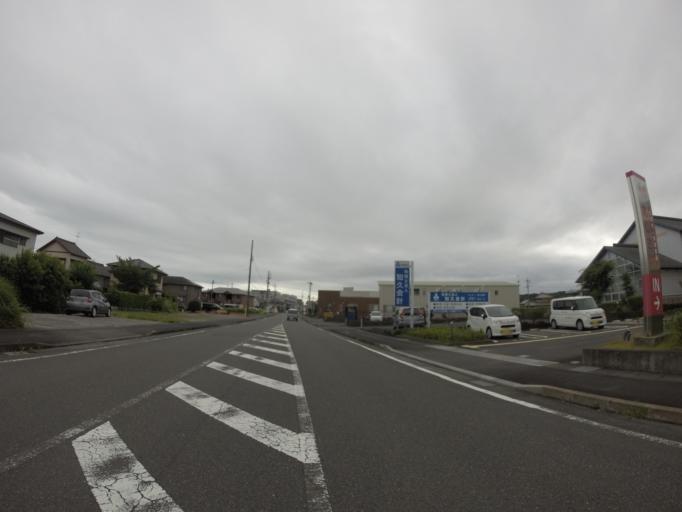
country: JP
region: Shizuoka
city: Shimada
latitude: 34.7589
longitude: 138.2404
